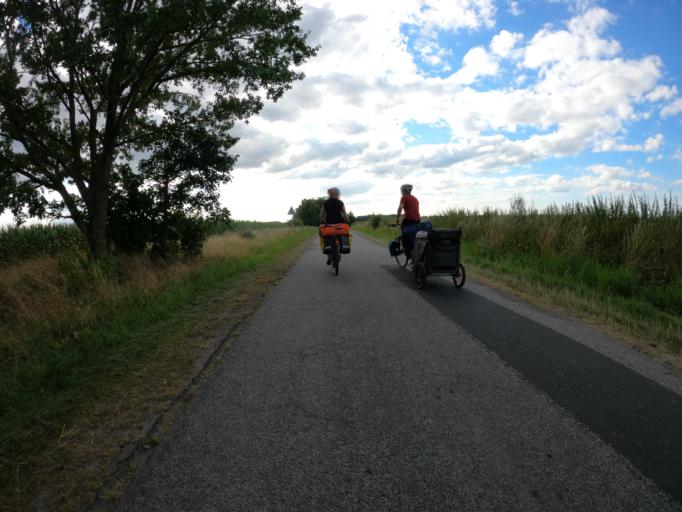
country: PL
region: West Pomeranian Voivodeship
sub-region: Powiat swidwinski
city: Swidwin
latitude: 53.7588
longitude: 15.6597
